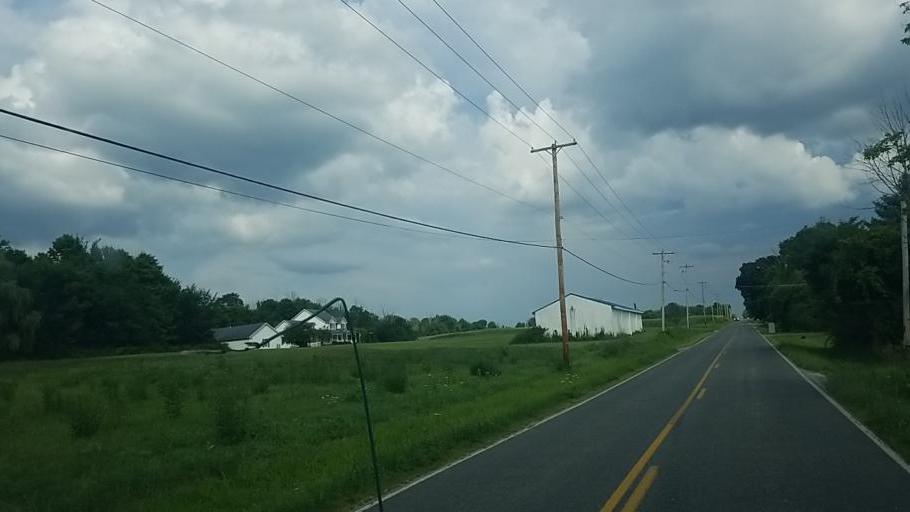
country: US
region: Ohio
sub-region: Medina County
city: Westfield Center
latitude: 41.0121
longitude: -81.9242
